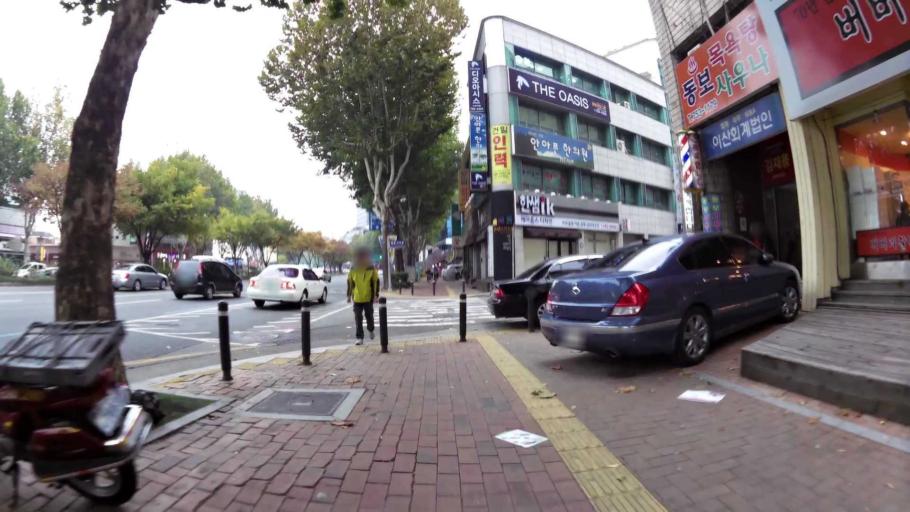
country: KR
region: Daegu
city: Daegu
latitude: 35.8604
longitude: 128.6103
